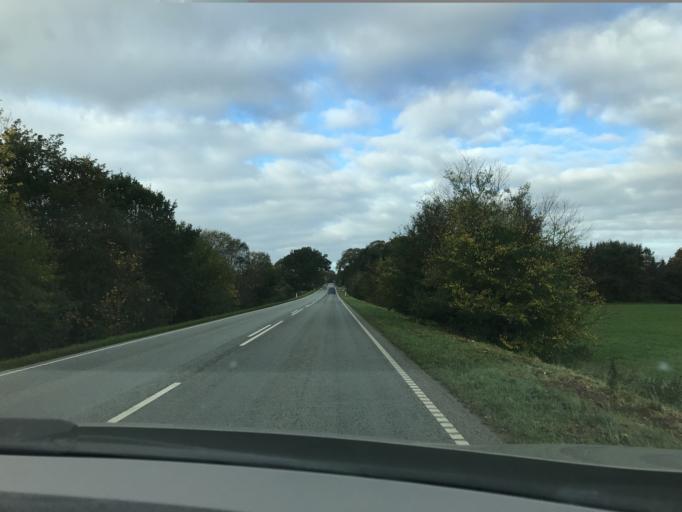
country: DK
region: South Denmark
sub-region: Vejle Kommune
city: Egtved
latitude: 55.5768
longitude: 9.3815
